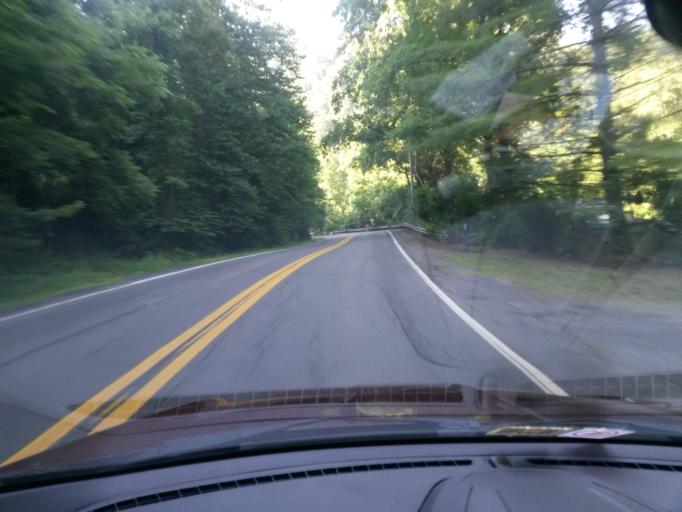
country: US
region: West Virginia
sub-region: Wyoming County
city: Pineville
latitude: 37.5200
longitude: -81.5880
